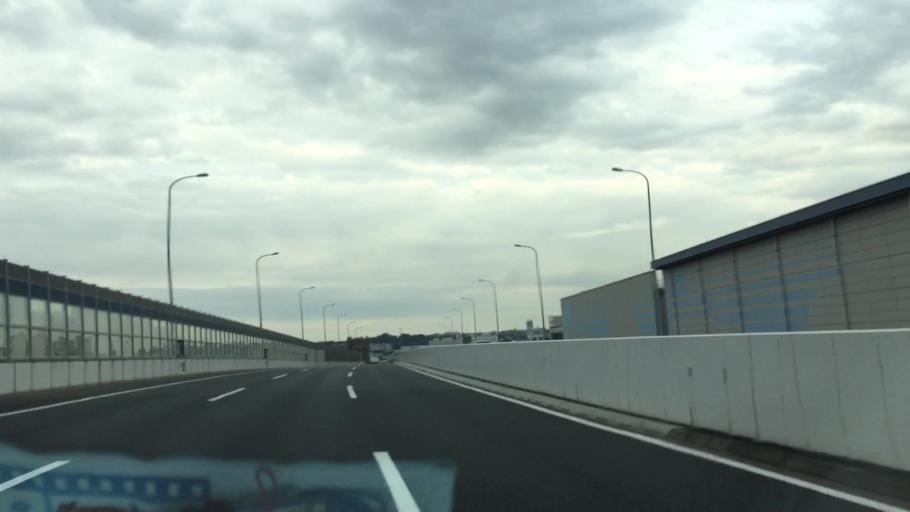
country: JP
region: Kanagawa
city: Yokohama
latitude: 35.3972
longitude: 139.6171
